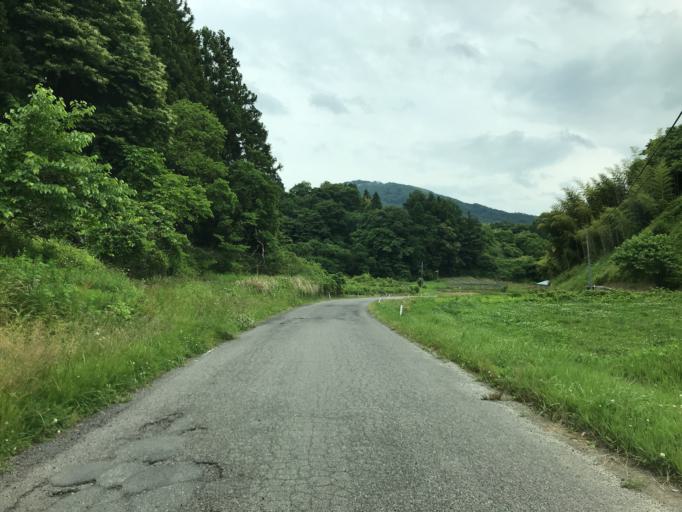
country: JP
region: Fukushima
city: Miharu
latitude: 37.3958
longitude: 140.5361
